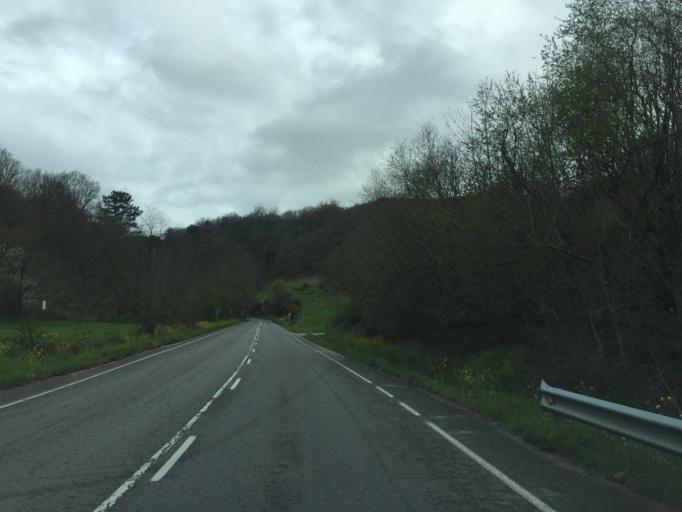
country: ES
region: Asturias
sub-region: Province of Asturias
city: Carrena
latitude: 43.3170
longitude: -4.8577
